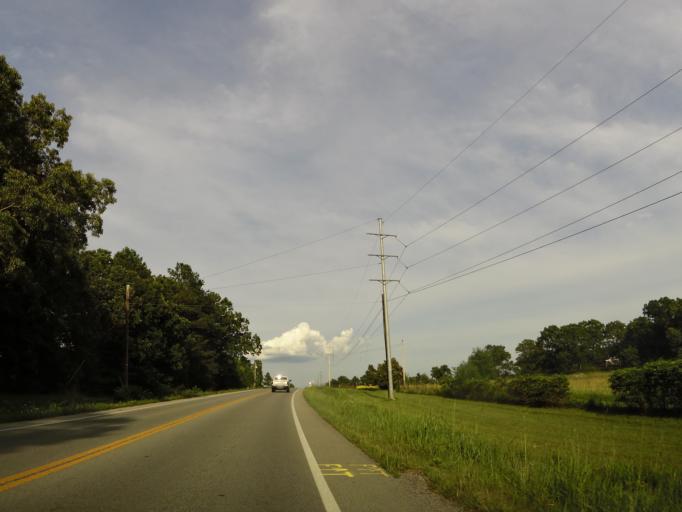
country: US
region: Tennessee
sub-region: Humphreys County
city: McEwen
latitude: 36.0938
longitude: -87.5406
